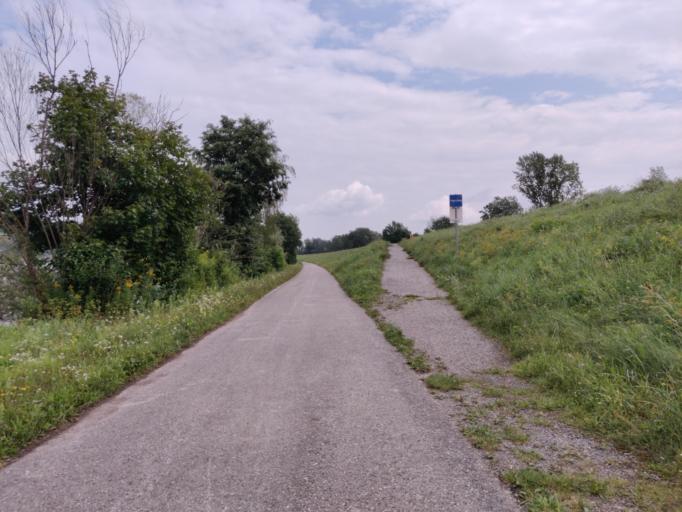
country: AT
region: Lower Austria
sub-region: Politischer Bezirk Melk
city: Marbach an der Donau
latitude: 48.2119
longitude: 15.1631
